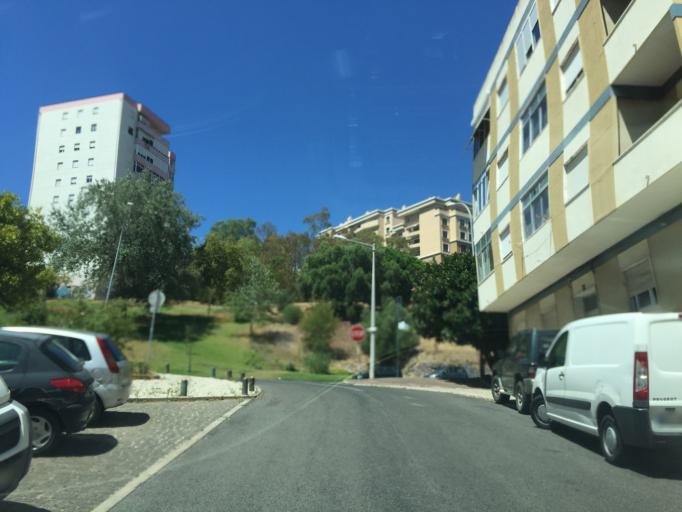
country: PT
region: Lisbon
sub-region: Odivelas
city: Povoa de Santo Adriao
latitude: 38.8147
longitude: -9.1568
